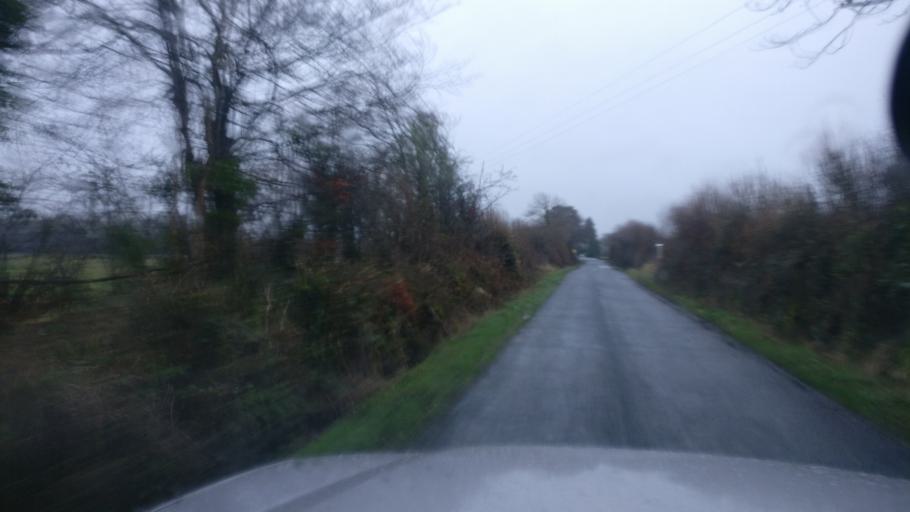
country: IE
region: Connaught
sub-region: County Galway
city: Ballinasloe
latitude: 53.3183
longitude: -8.3742
